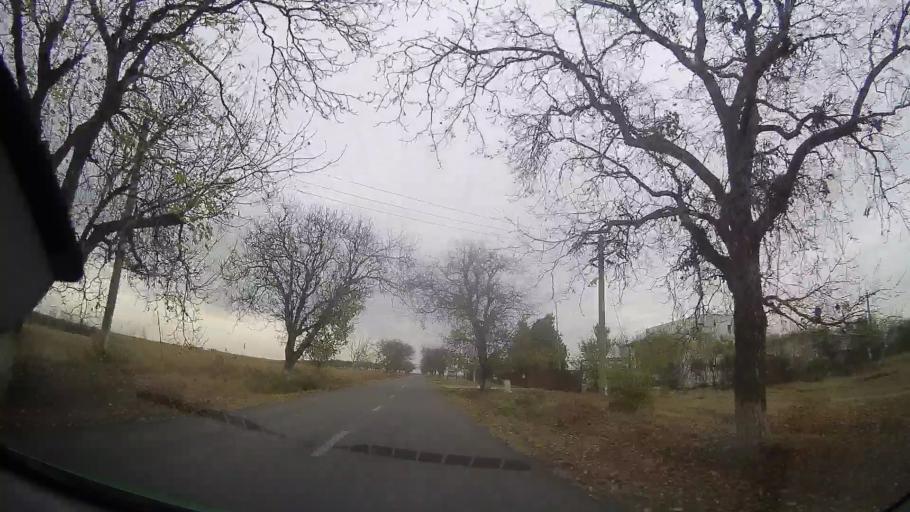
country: RO
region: Prahova
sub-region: Comuna Vadu Sapat
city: Vadu Sapat
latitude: 45.0228
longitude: 26.3914
